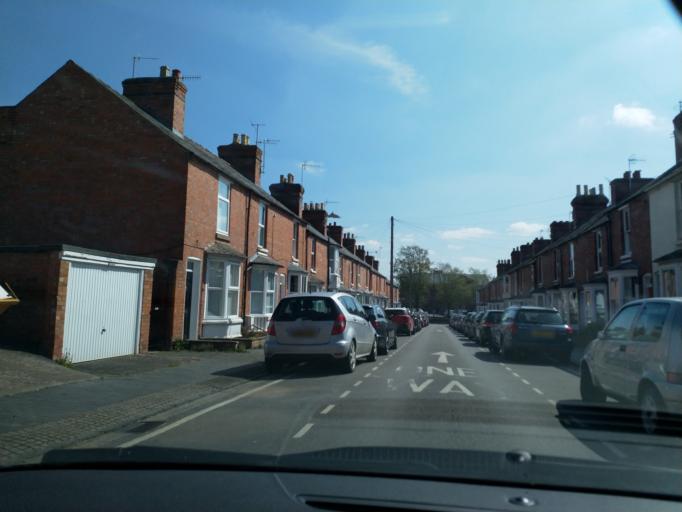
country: GB
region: England
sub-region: Warwickshire
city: Stratford-upon-Avon
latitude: 52.1924
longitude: -1.7138
